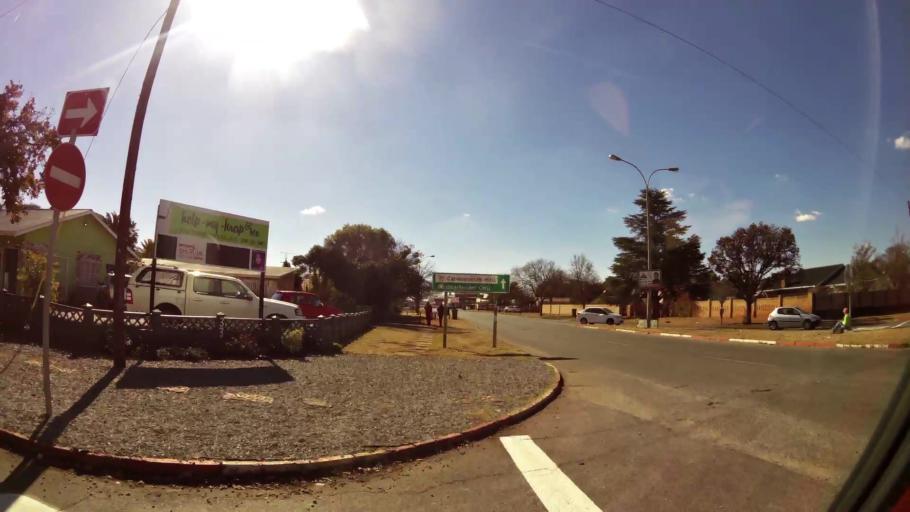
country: ZA
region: Gauteng
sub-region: West Rand District Municipality
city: Carletonville
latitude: -26.3522
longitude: 27.3898
